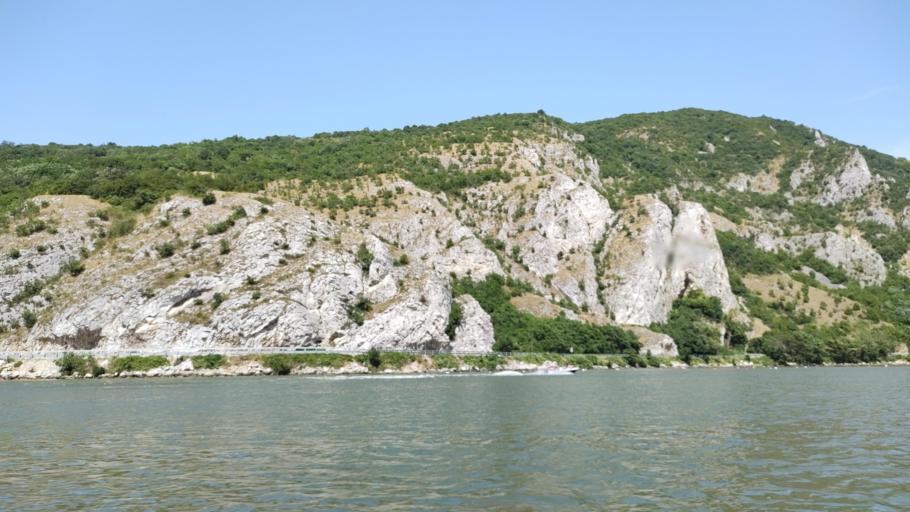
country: RO
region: Caras-Severin
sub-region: Comuna Pescari
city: Coronini
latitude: 44.6638
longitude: 21.6954
